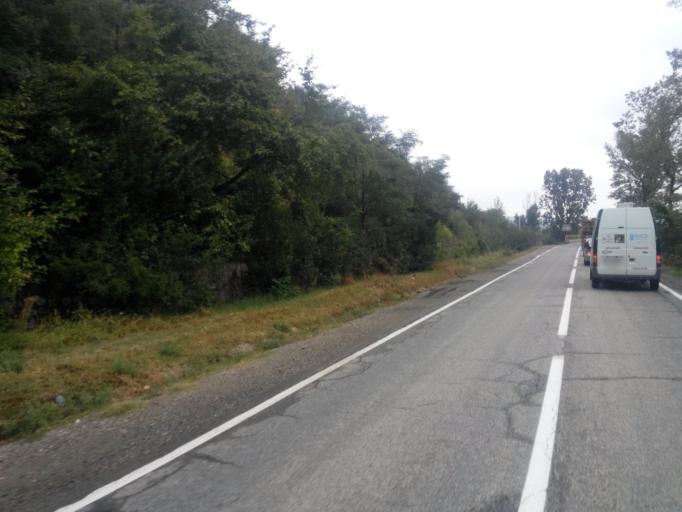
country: RO
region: Cluj
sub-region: Comuna Moldovenesti
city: Moldovenesti
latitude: 46.5106
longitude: 23.6596
